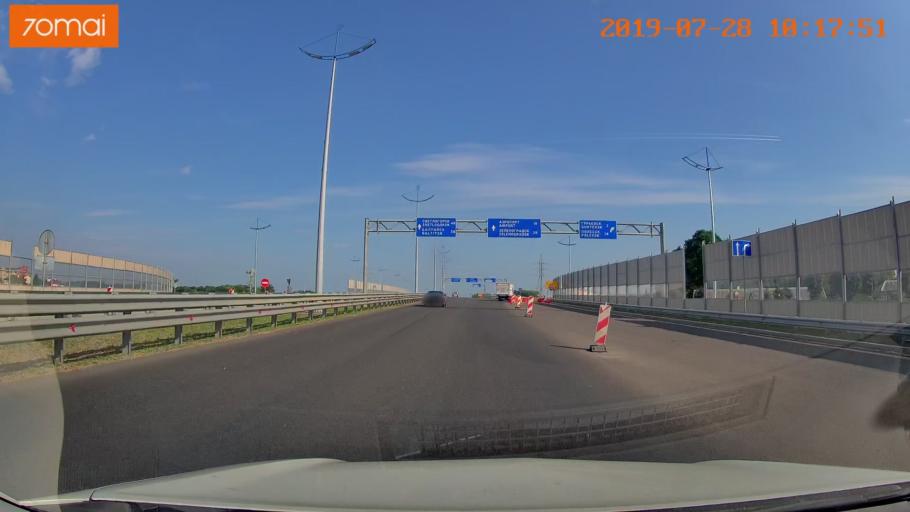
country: RU
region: Kaliningrad
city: Maloye Isakovo
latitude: 54.7442
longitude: 20.5924
